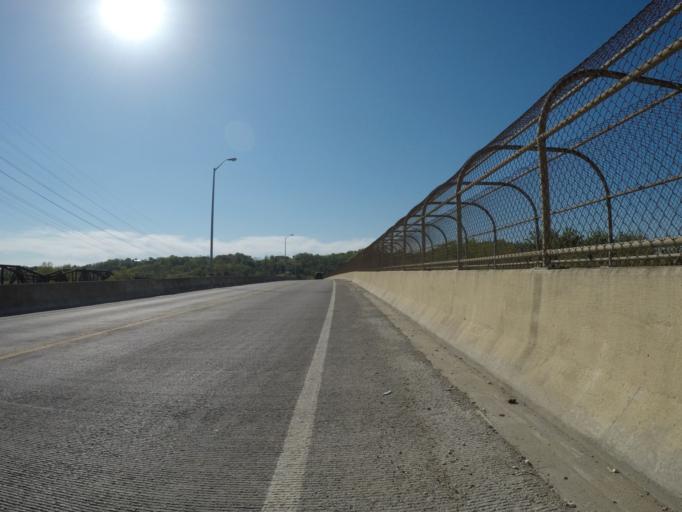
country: US
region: Kentucky
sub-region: Boyd County
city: Catlettsburg
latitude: 38.4040
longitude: -82.5934
